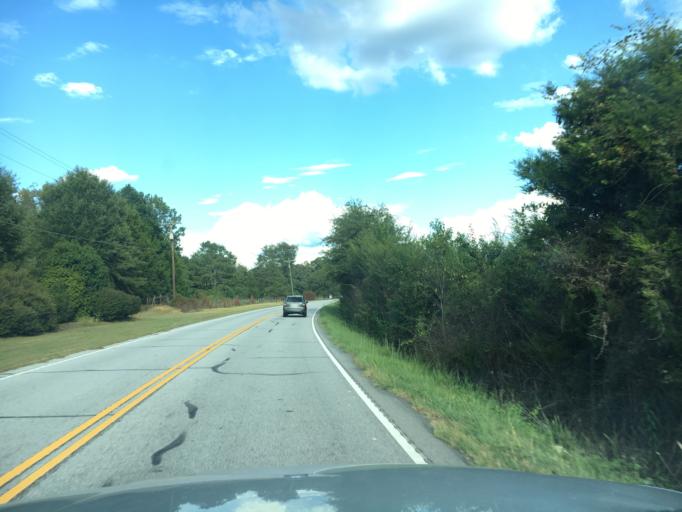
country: US
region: South Carolina
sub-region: Greenwood County
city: Ware Shoals
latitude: 34.5244
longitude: -82.1824
